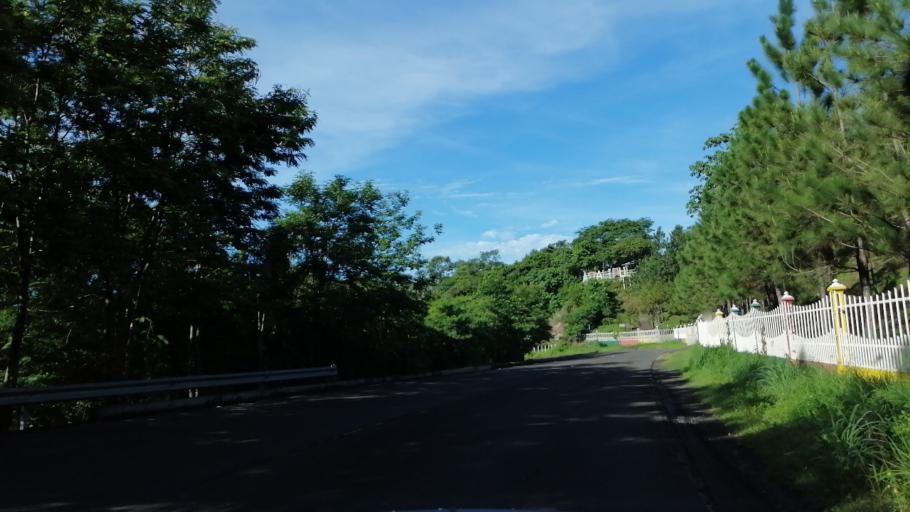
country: SV
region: Morazan
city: Cacaopera
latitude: 13.7812
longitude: -88.1028
